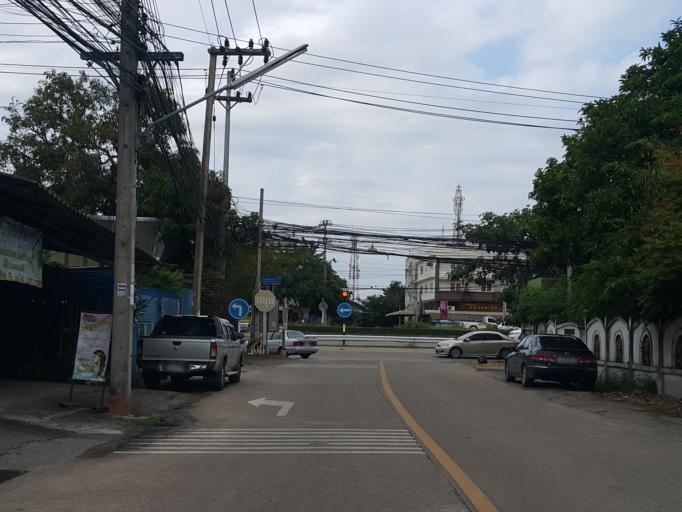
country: TH
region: Lampang
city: Lampang
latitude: 18.2800
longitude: 99.4907
